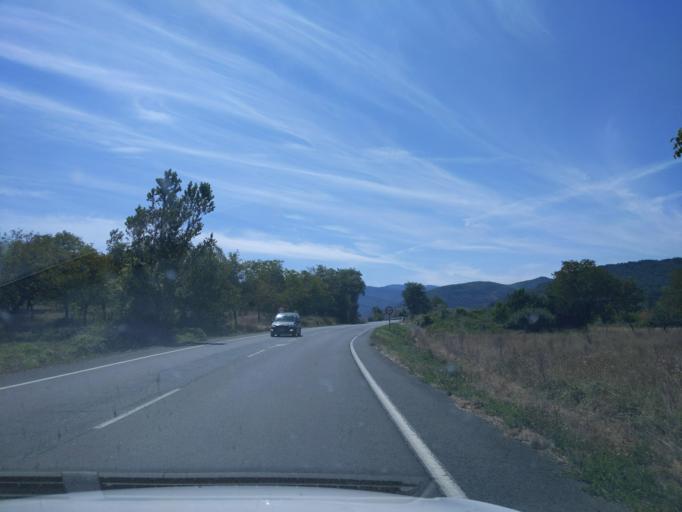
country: ES
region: La Rioja
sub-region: Provincia de La Rioja
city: Ojacastro
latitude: 42.3655
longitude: -2.9837
